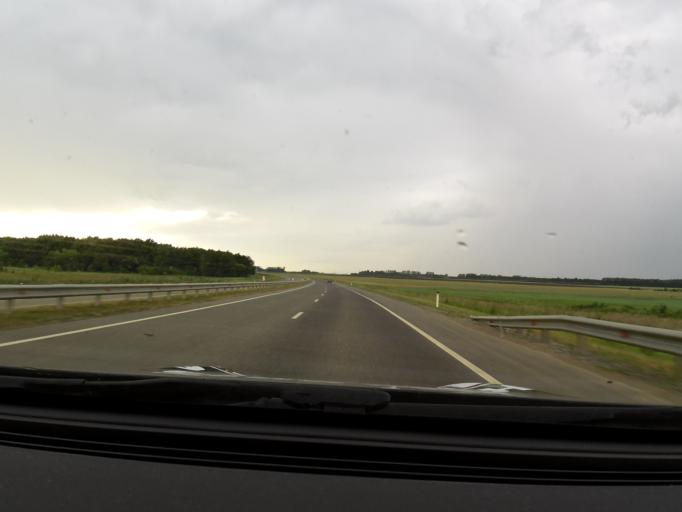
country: RU
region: Bashkortostan
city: Kushnarenkovo
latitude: 55.0675
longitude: 55.3487
